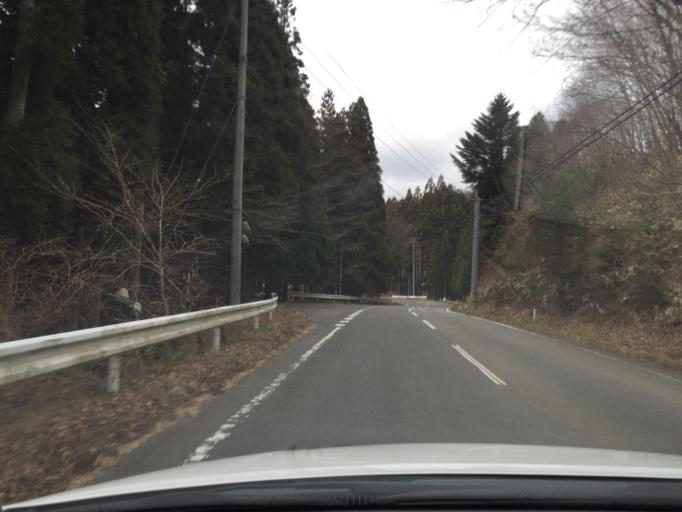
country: JP
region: Fukushima
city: Iwaki
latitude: 37.1864
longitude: 140.7119
